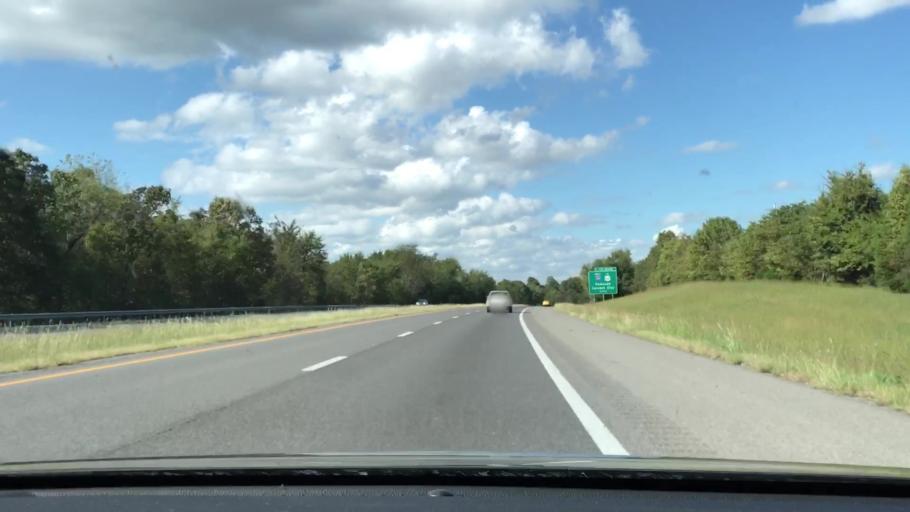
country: US
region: Kentucky
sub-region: Marshall County
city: Calvert City
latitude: 36.9470
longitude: -88.3492
